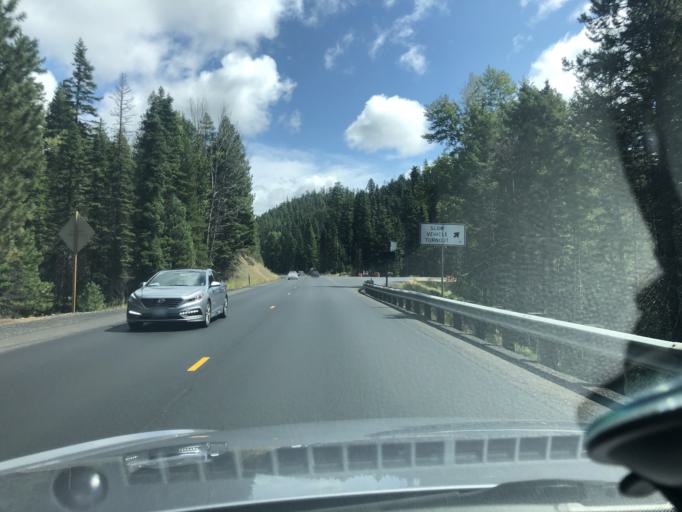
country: US
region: Washington
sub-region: Chelan County
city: Cashmere
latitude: 47.3301
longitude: -120.6485
